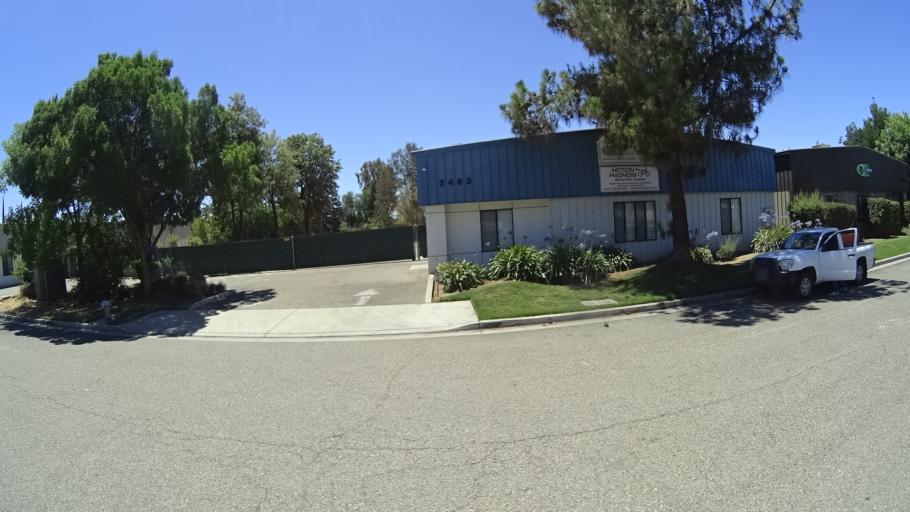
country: US
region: California
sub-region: Fresno County
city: West Park
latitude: 36.8014
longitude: -119.8552
